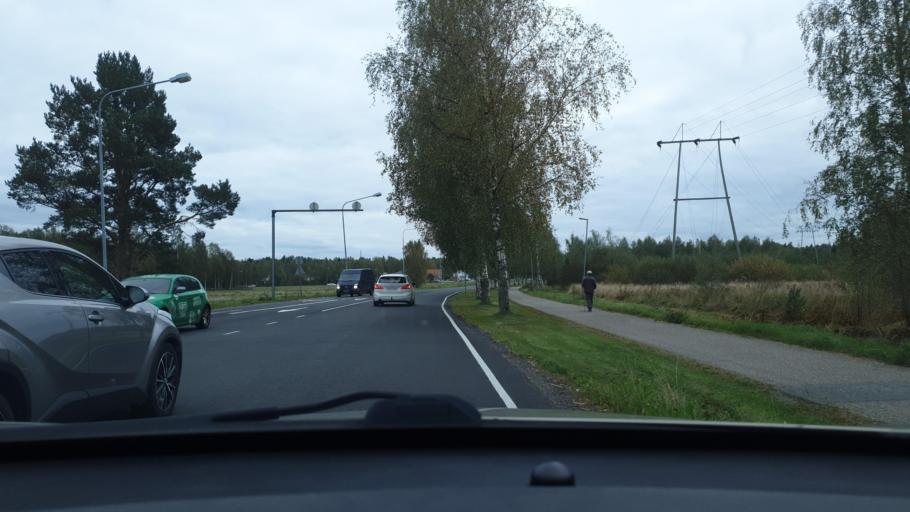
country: FI
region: Ostrobothnia
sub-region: Vaasa
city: Teeriniemi
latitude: 63.0896
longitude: 21.6997
